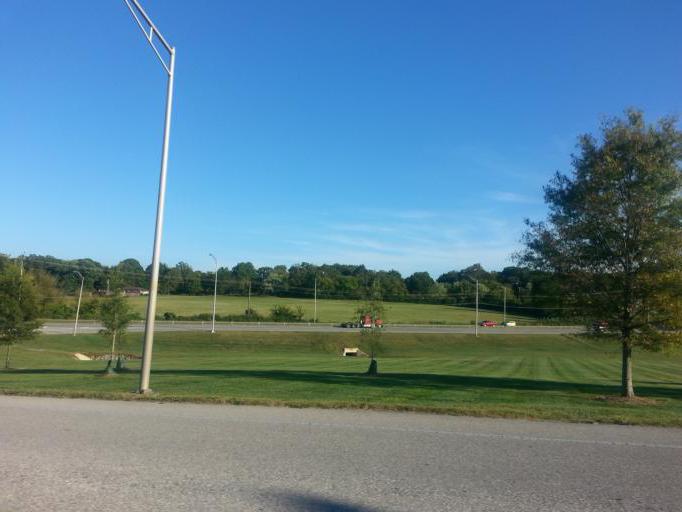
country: US
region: Tennessee
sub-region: Blount County
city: Alcoa
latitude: 35.8042
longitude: -83.9889
